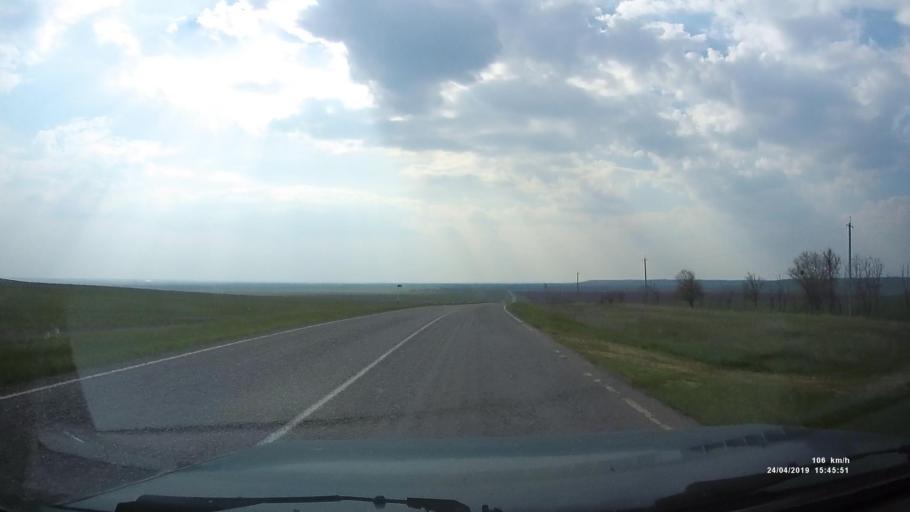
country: RU
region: Kalmykiya
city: Yashalta
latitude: 46.5919
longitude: 42.7281
